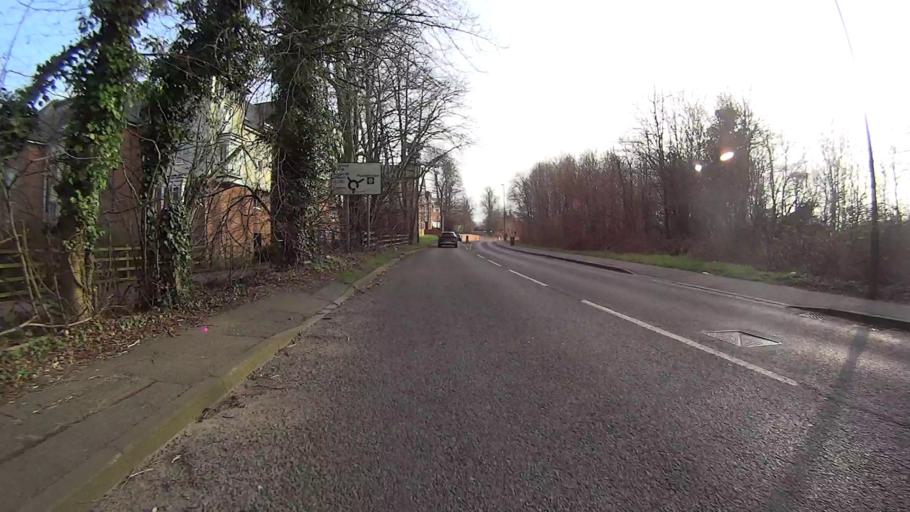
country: GB
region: England
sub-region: West Sussex
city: Maidenbower
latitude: 51.1132
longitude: -0.1466
